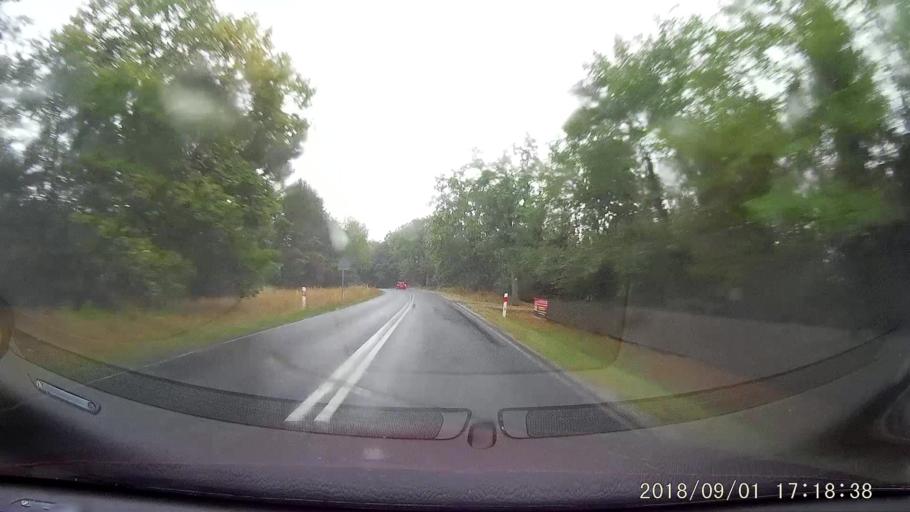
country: PL
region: Lubusz
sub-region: Powiat zielonogorski
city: Nowogrod Bobrzanski
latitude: 51.7376
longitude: 15.2721
